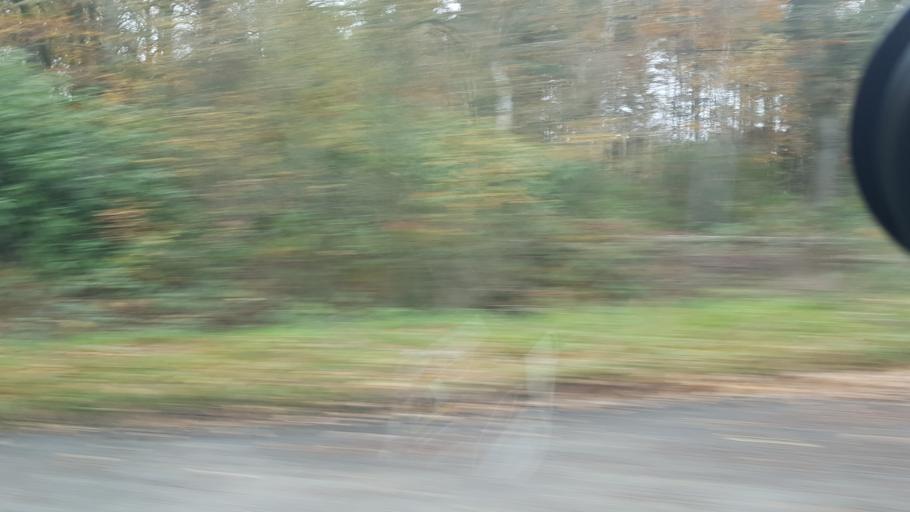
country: GB
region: England
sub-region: Hampshire
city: Fleet
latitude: 51.3101
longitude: -0.8103
